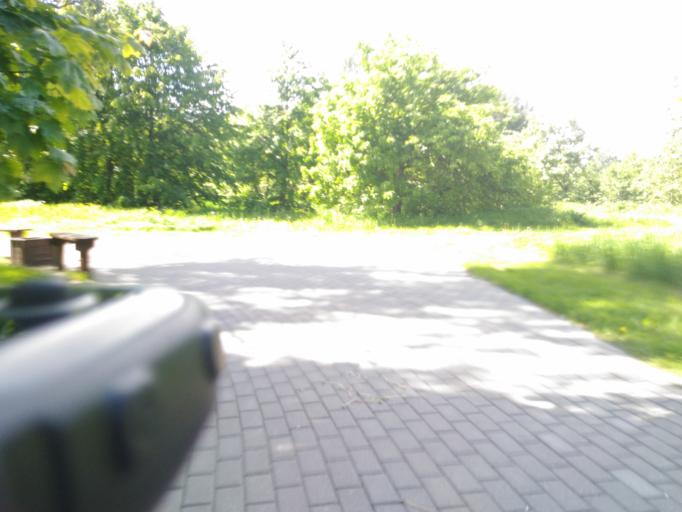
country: RU
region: Moscow
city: Shchukino
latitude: 55.7739
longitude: 37.4158
